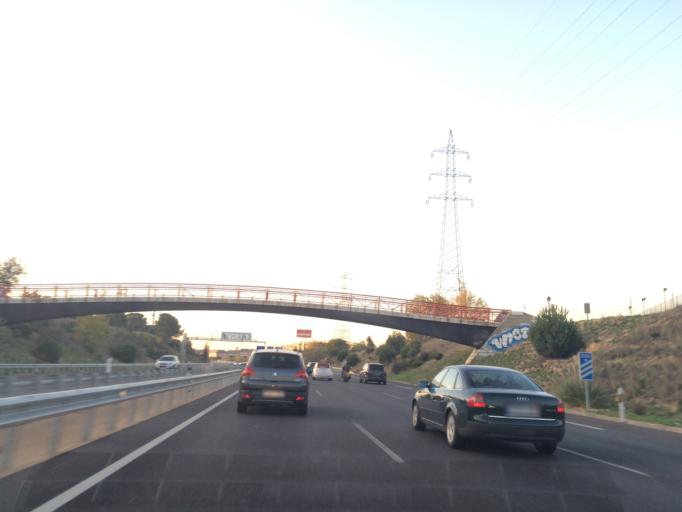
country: ES
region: Madrid
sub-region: Provincia de Madrid
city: Majadahonda
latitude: 40.4451
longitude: -3.8525
